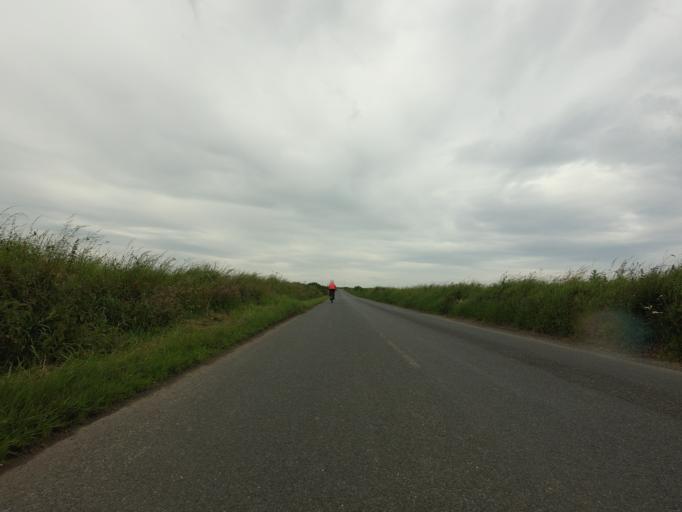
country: GB
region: Scotland
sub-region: Aberdeenshire
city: Whitehills
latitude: 57.6703
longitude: -2.6072
